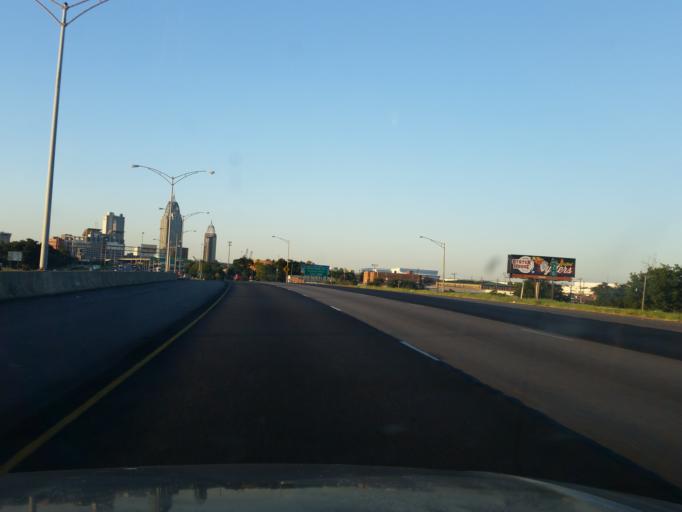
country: US
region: Alabama
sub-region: Mobile County
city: Mobile
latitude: 30.6753
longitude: -88.0441
